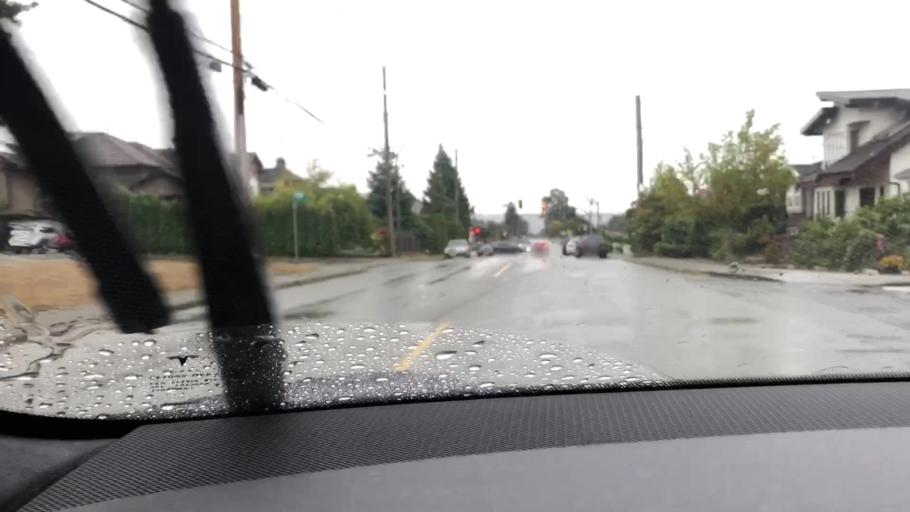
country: CA
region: British Columbia
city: New Westminster
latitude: 49.2283
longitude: -122.9135
